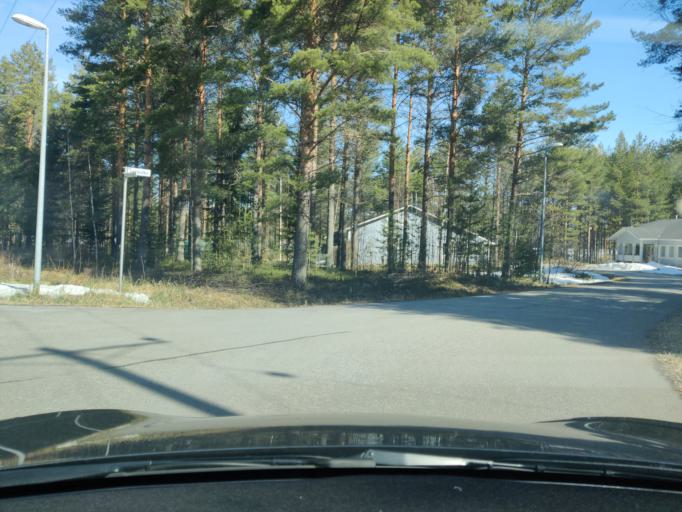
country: FI
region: Northern Savo
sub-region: Kuopio
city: Vehmersalmi
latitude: 62.7711
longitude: 27.9858
